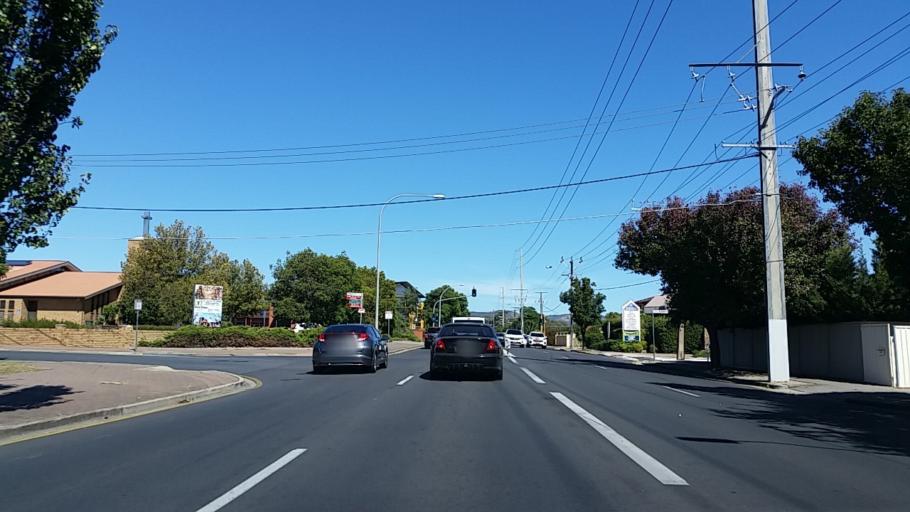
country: AU
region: South Australia
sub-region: Campbelltown
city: Campbelltown
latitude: -34.8813
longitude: 138.6737
